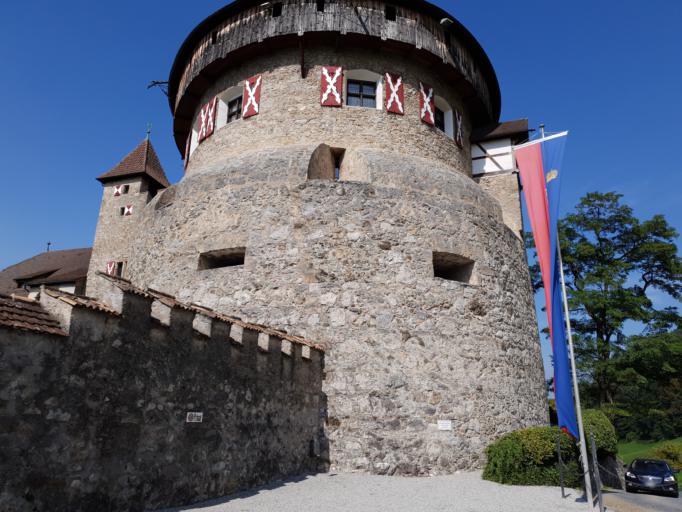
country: LI
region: Vaduz
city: Vaduz
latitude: 47.1391
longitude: 9.5247
